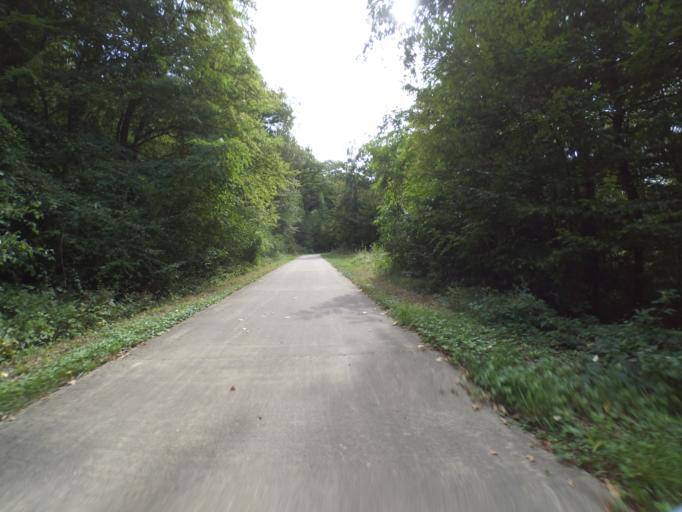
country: LU
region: Grevenmacher
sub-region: Canton de Remich
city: Bous
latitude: 49.5303
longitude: 6.3286
